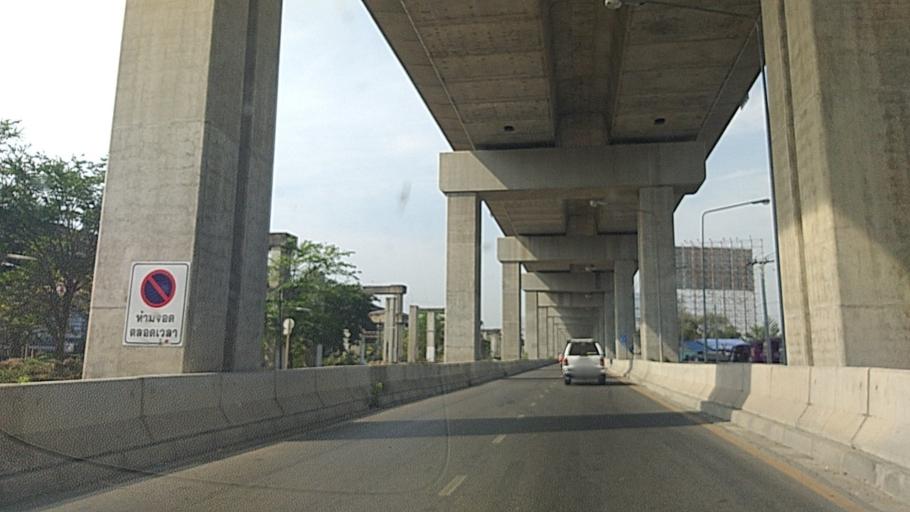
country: TH
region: Bangkok
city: Chatuchak
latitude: 13.8462
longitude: 100.5600
